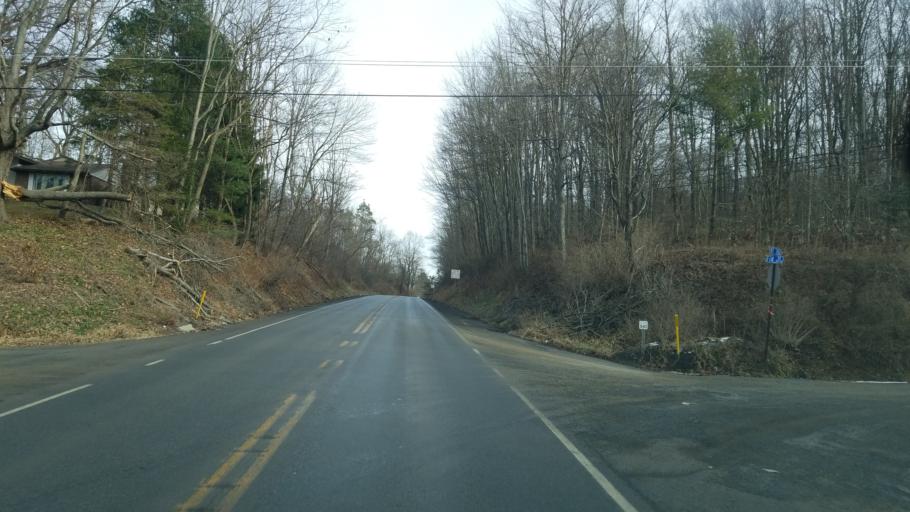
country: US
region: Pennsylvania
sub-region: Indiana County
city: Clymer
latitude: 40.7036
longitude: -78.9854
